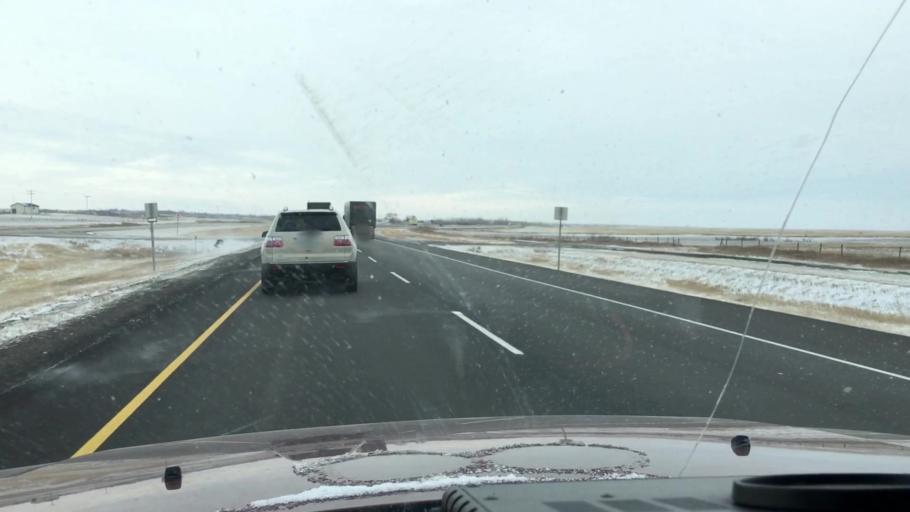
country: CA
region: Saskatchewan
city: Saskatoon
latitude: 51.7830
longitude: -106.4787
